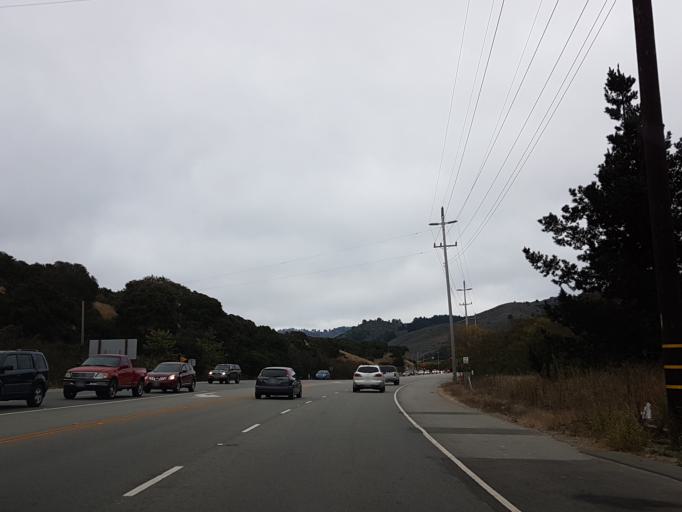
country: US
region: California
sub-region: Monterey County
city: Del Rey Oaks
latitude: 36.5803
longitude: -121.8273
